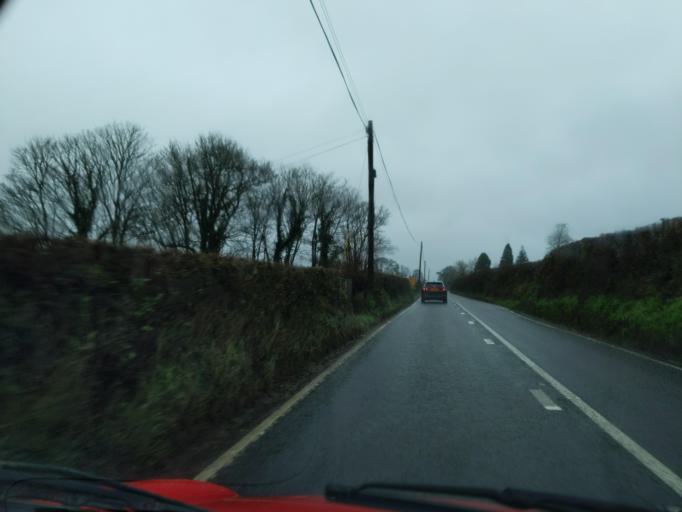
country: GB
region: England
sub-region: Cornwall
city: Launceston
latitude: 50.6060
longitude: -4.3384
